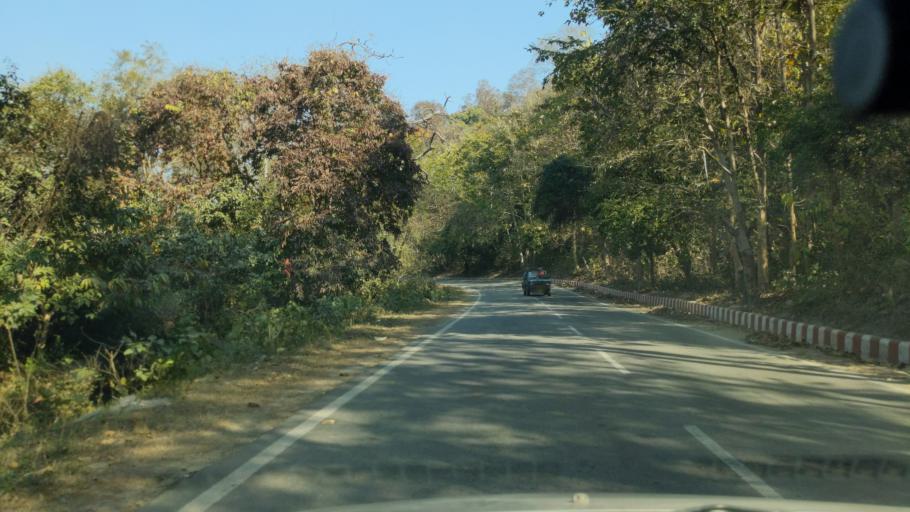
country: IN
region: Uttarakhand
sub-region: Naini Tal
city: Ramnagar
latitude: 29.3924
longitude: 79.1379
